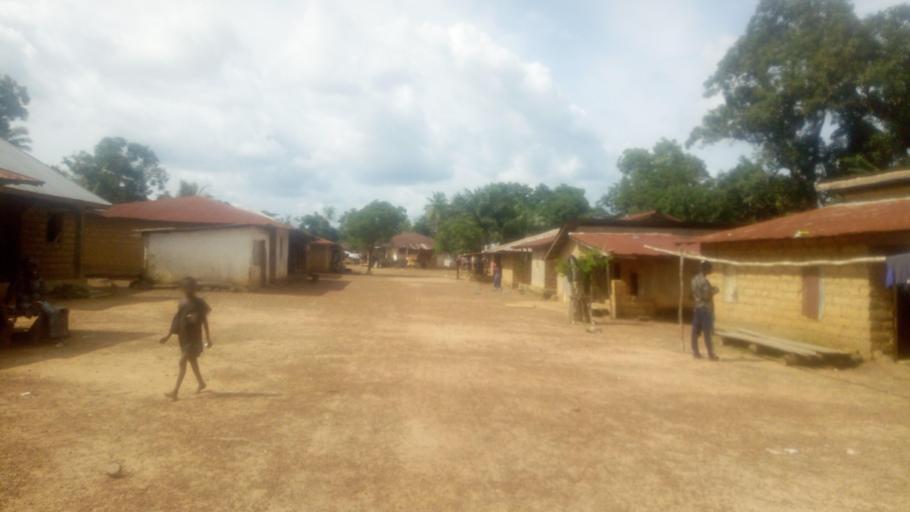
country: SL
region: Northern Province
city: Magburaka
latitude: 8.6877
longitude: -12.0639
